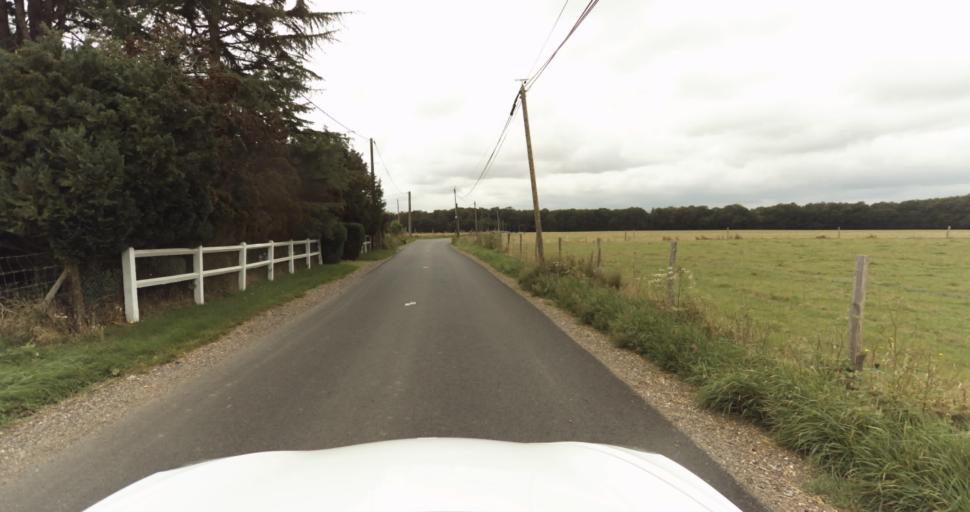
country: FR
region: Haute-Normandie
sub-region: Departement de l'Eure
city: Damville
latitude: 48.9293
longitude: 1.0834
